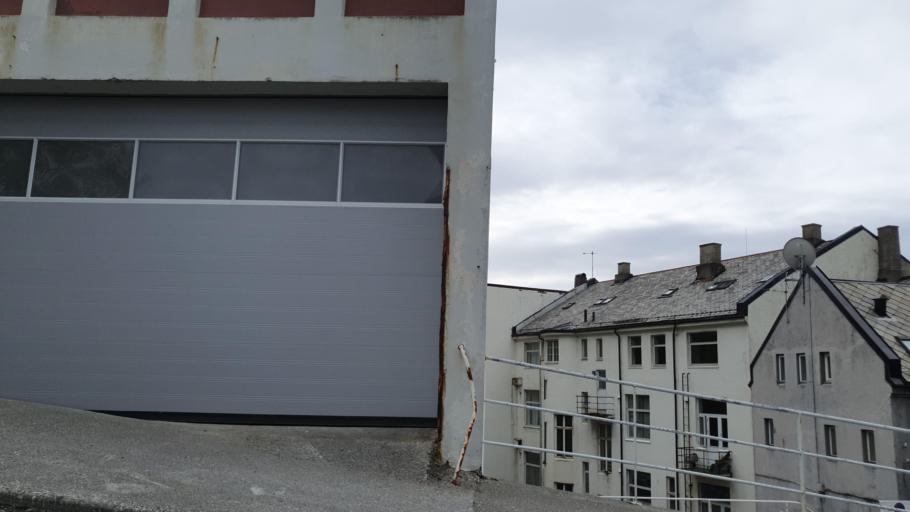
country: NO
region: More og Romsdal
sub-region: Alesund
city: Alesund
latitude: 62.4734
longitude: 6.1589
